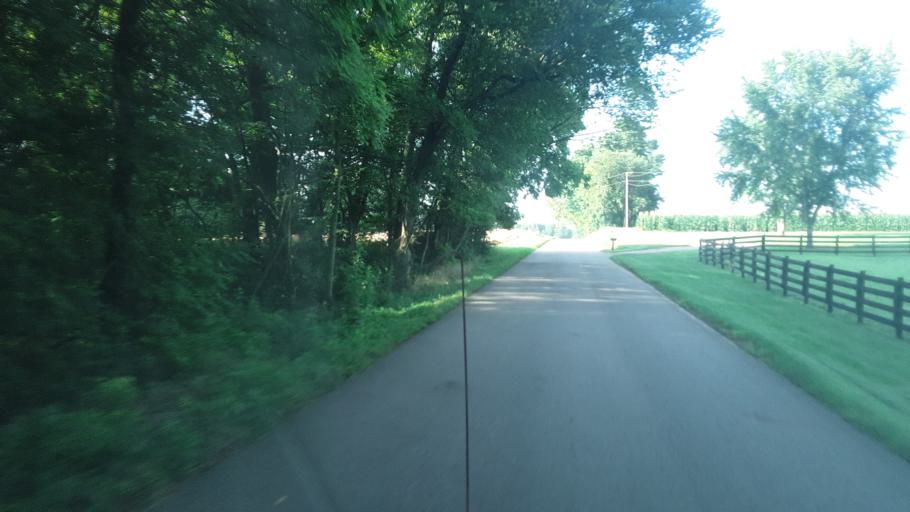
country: US
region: Kentucky
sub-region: Todd County
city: Guthrie
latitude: 36.6765
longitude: -87.1690
